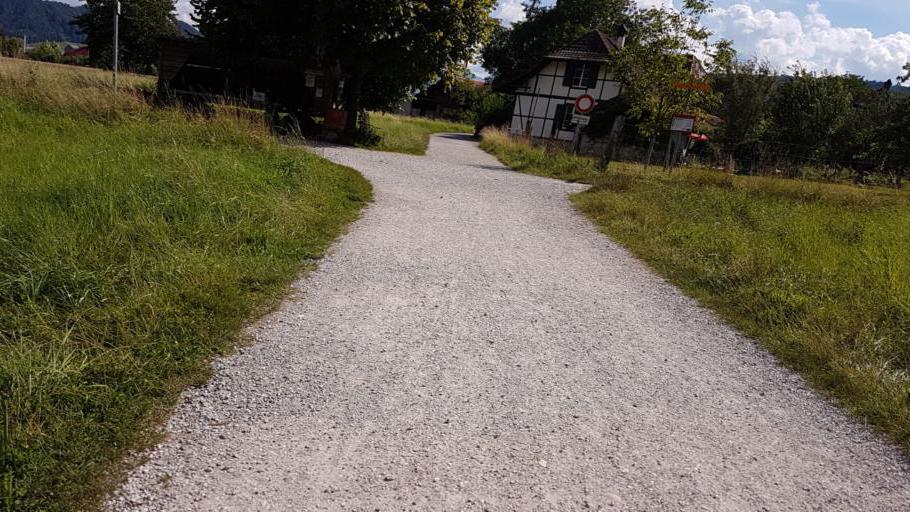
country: CH
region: Bern
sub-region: Bern-Mittelland District
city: Muri
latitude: 46.9174
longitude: 7.4998
